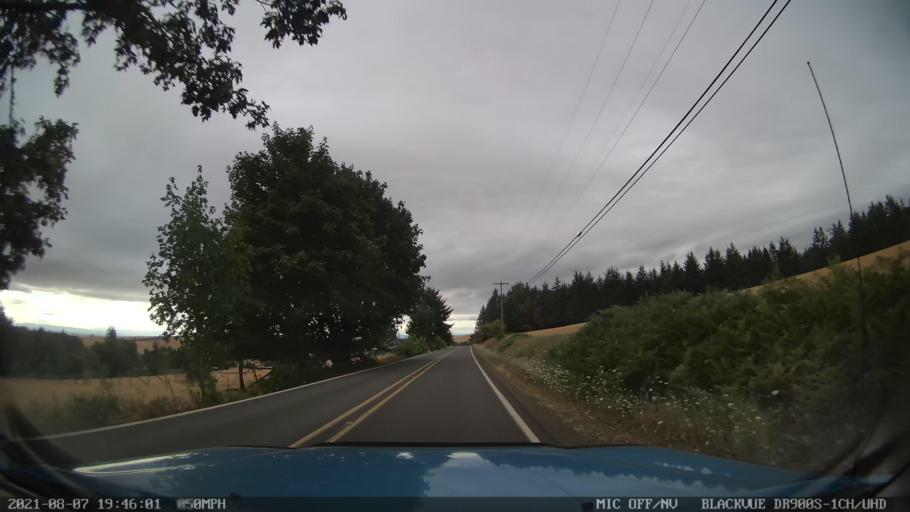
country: US
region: Oregon
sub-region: Marion County
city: Silverton
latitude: 44.9540
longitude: -122.7007
